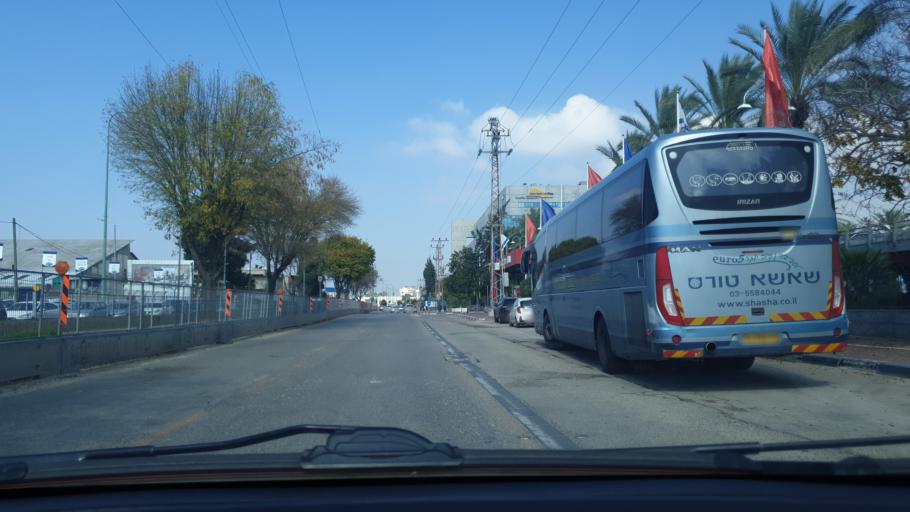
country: IL
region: Tel Aviv
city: Azor
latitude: 32.0094
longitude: 34.8080
